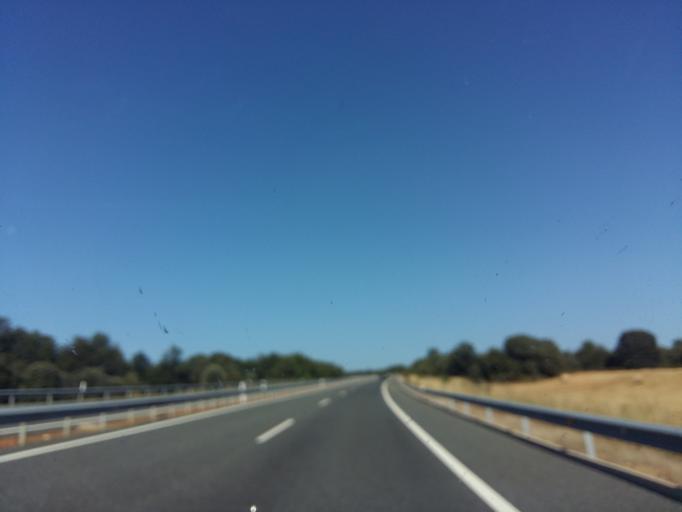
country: ES
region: Castille and Leon
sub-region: Provincia de Leon
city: San Justo de la Vega
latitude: 42.4439
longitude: -5.9654
